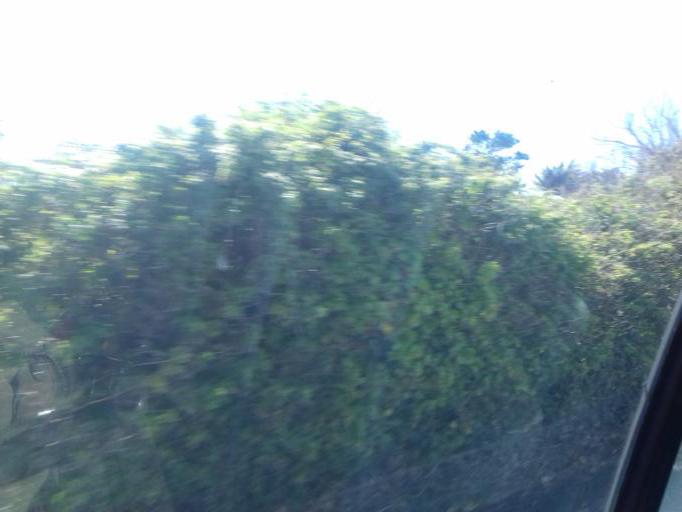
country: IE
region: Munster
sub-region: Waterford
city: Dunmore East
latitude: 52.1360
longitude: -6.9179
